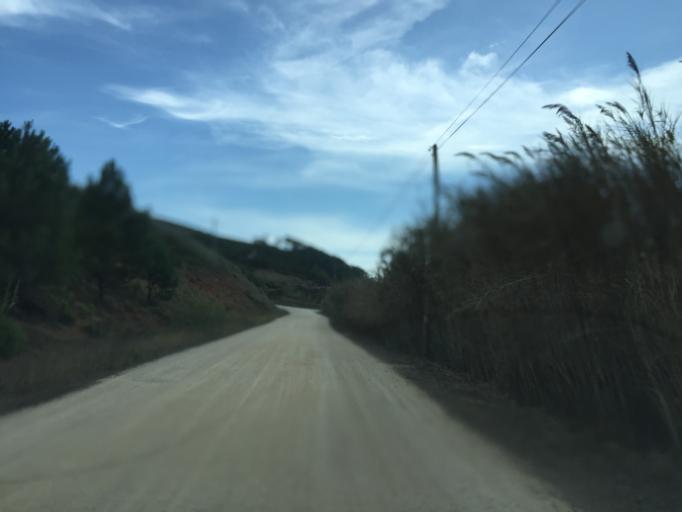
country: PT
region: Lisbon
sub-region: Torres Vedras
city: A dos Cunhados
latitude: 39.1814
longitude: -9.3449
